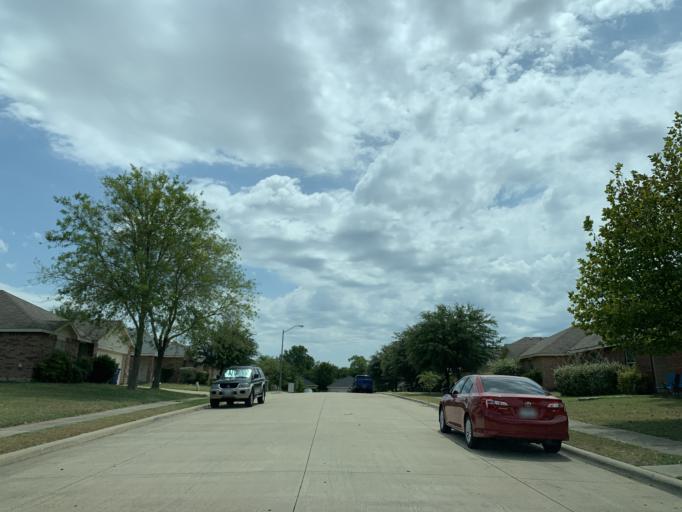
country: US
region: Texas
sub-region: Dallas County
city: DeSoto
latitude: 32.6579
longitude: -96.8144
